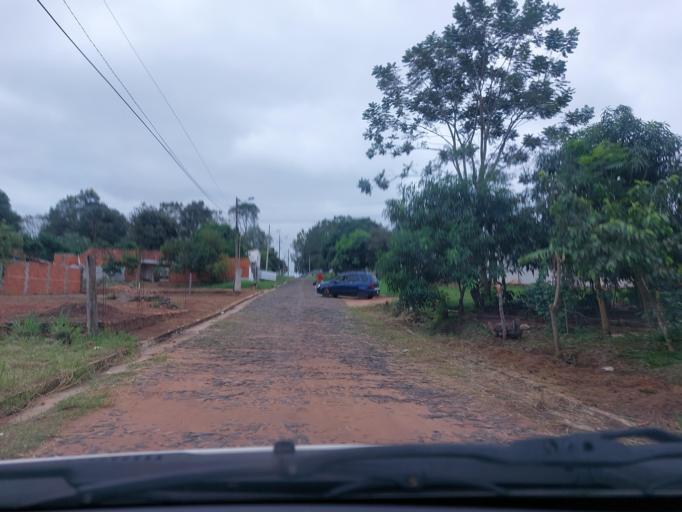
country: PY
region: San Pedro
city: Guayaybi
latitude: -24.6669
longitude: -56.4325
